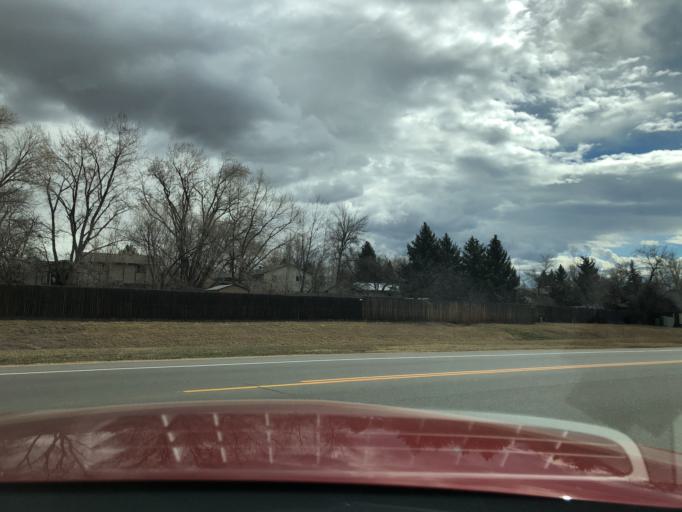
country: US
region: Colorado
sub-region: Boulder County
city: Gunbarrel
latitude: 40.0590
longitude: -105.1785
